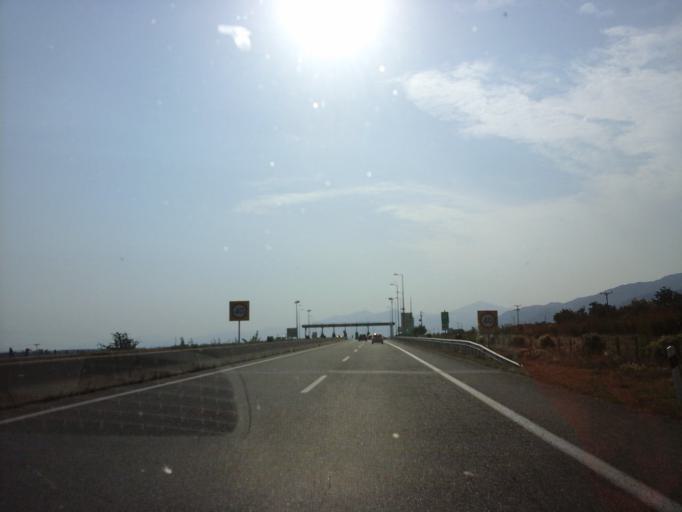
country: GR
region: East Macedonia and Thrace
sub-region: Nomos Xanthis
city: Selero
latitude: 41.1203
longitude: 25.0837
